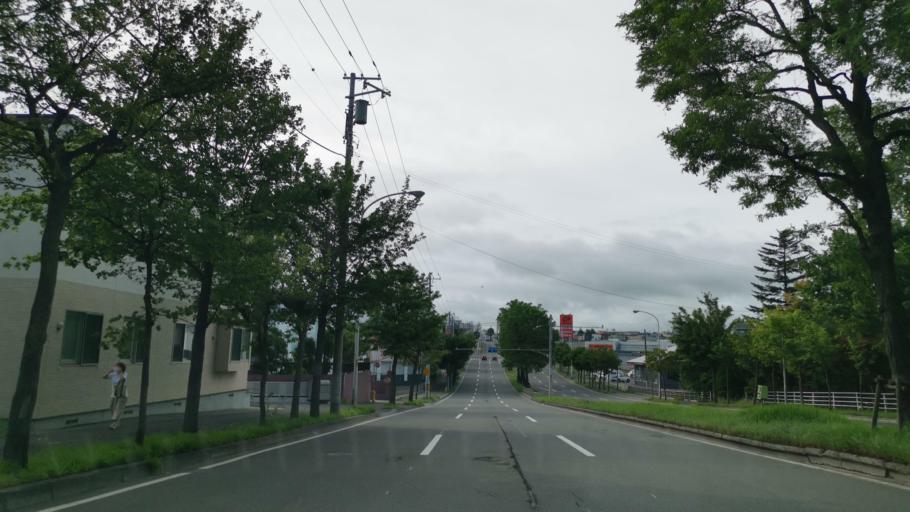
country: JP
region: Hokkaido
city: Sapporo
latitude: 43.0229
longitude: 141.3818
